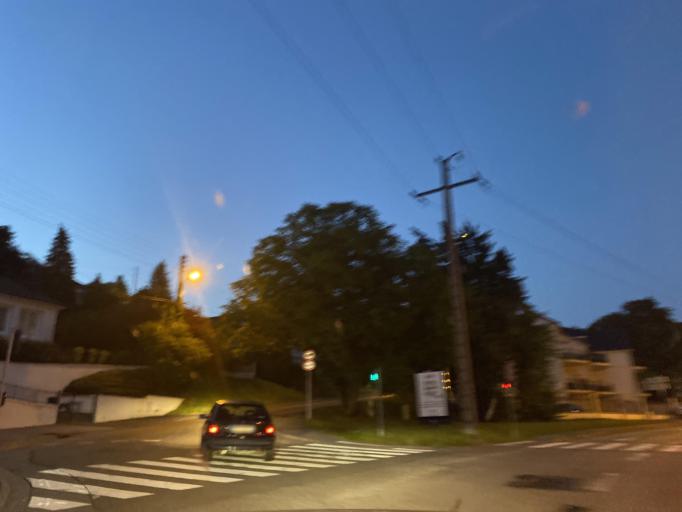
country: FR
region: Haute-Normandie
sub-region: Departement de l'Eure
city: Evreux
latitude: 49.0282
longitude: 1.1668
